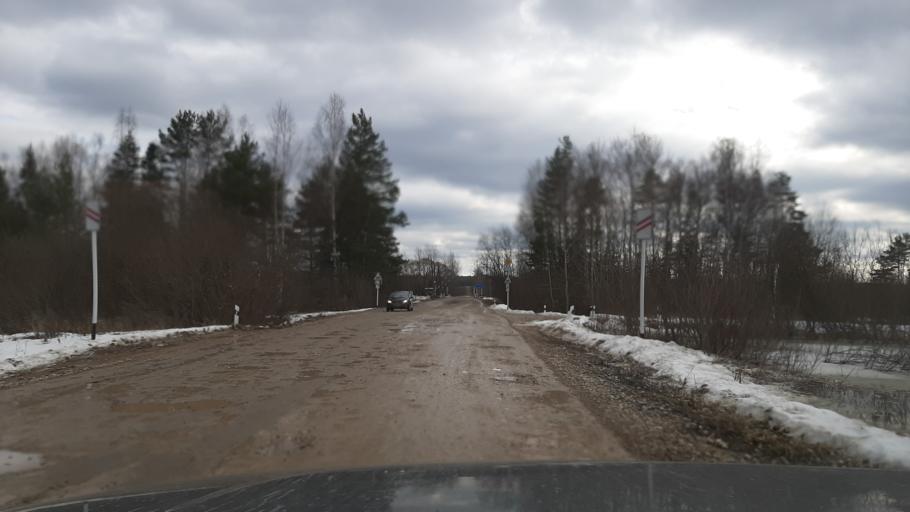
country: RU
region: Ivanovo
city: Teykovo
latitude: 56.8839
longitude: 40.6219
